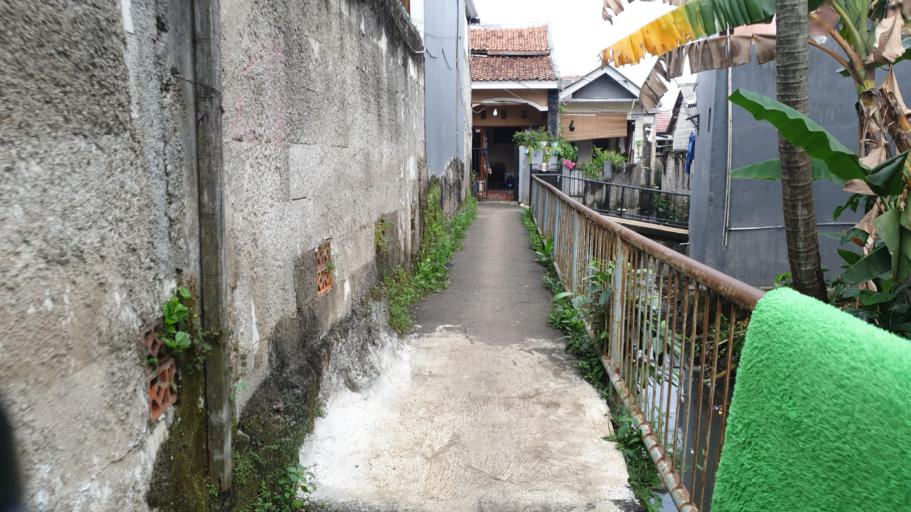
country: ID
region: West Java
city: Depok
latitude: -6.3329
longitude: 106.8217
